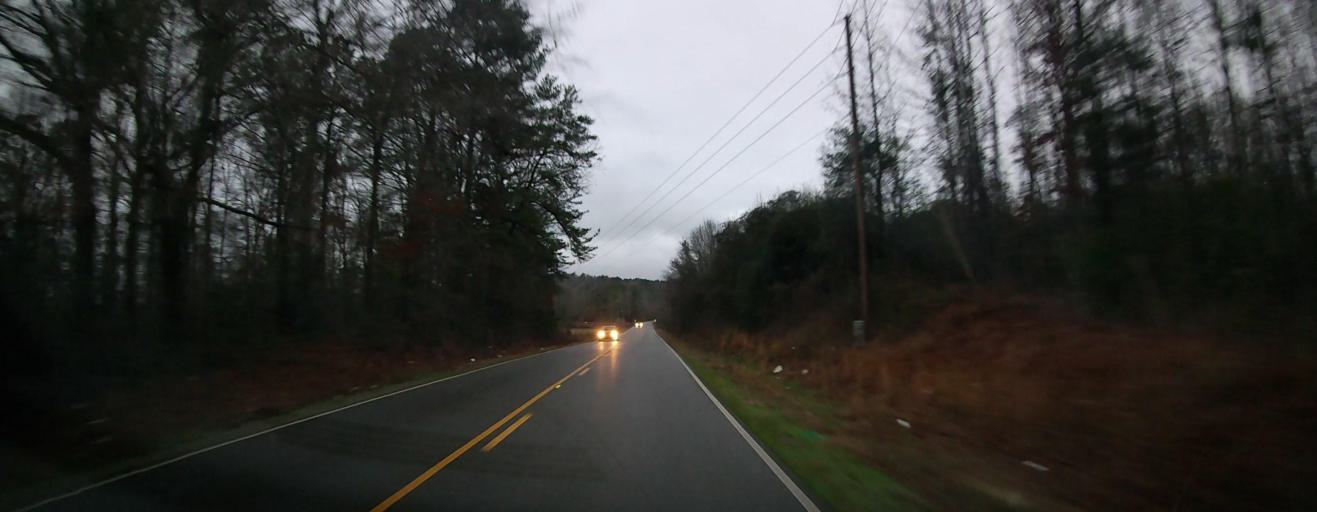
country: US
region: Alabama
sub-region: Tuscaloosa County
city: Vance
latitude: 33.1216
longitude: -87.2256
